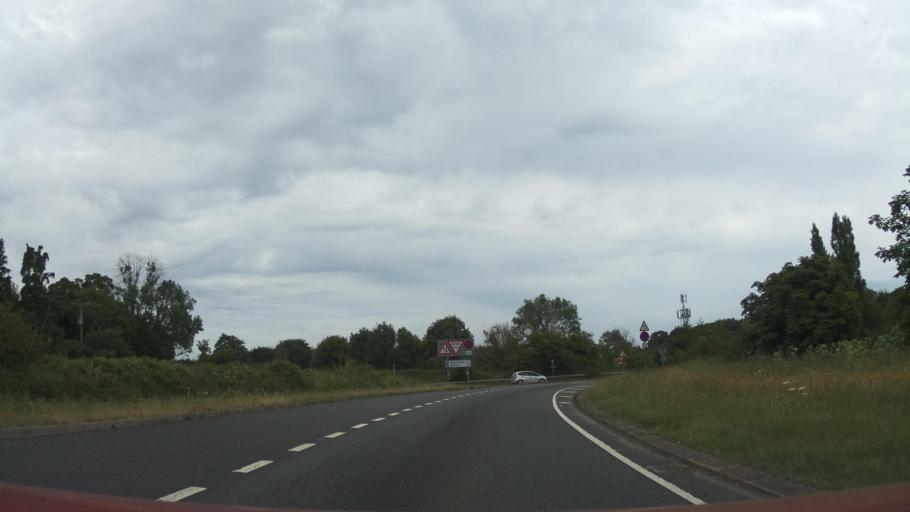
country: GB
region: England
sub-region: Devon
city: Ashburton
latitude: 50.5358
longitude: -3.7159
